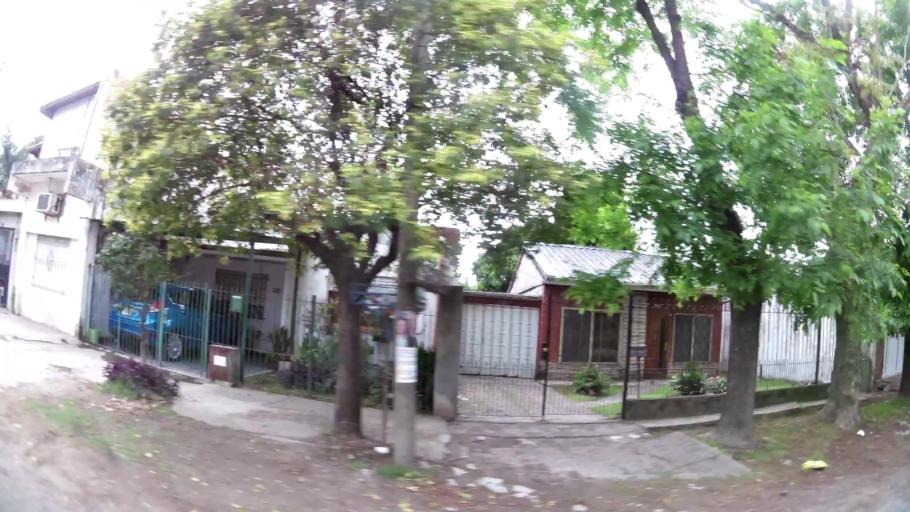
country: AR
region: Buenos Aires
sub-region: Partido de Quilmes
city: Quilmes
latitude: -34.7967
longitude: -58.2696
